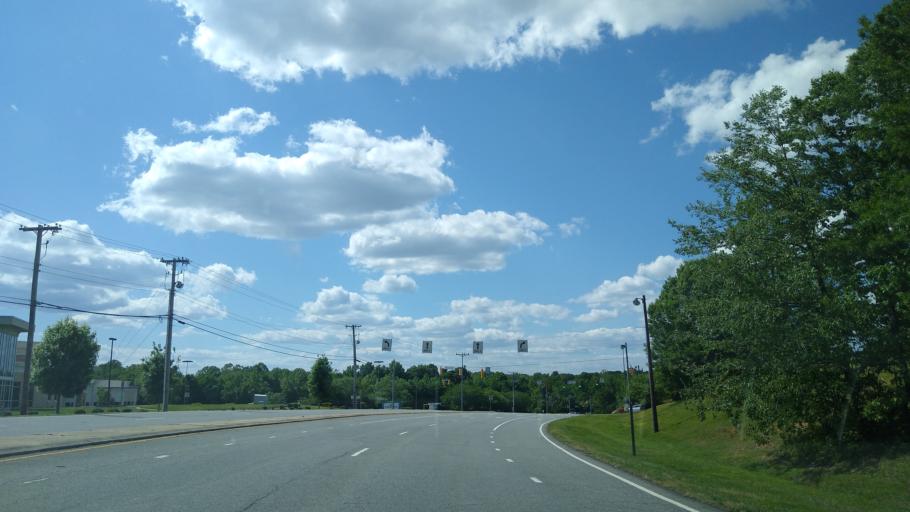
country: US
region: North Carolina
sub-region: Guilford County
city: High Point
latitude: 35.9897
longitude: -80.0092
